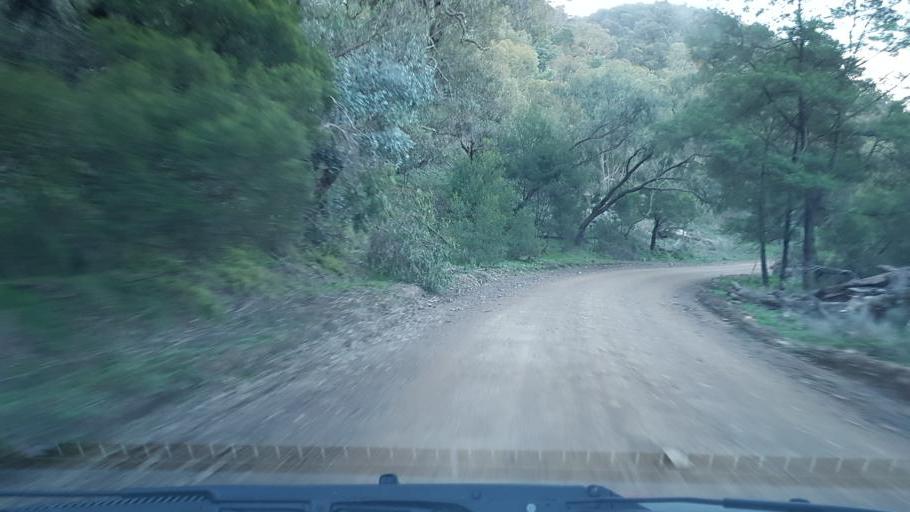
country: AU
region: New South Wales
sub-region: Palerang
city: Bungendore
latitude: -35.1618
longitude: 149.3927
